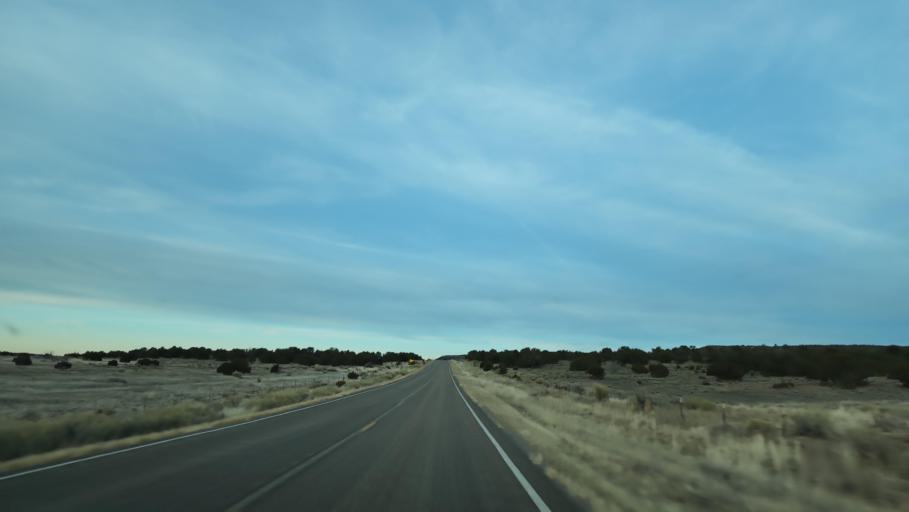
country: US
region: New Mexico
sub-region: Cibola County
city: Grants
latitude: 34.7190
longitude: -107.9816
